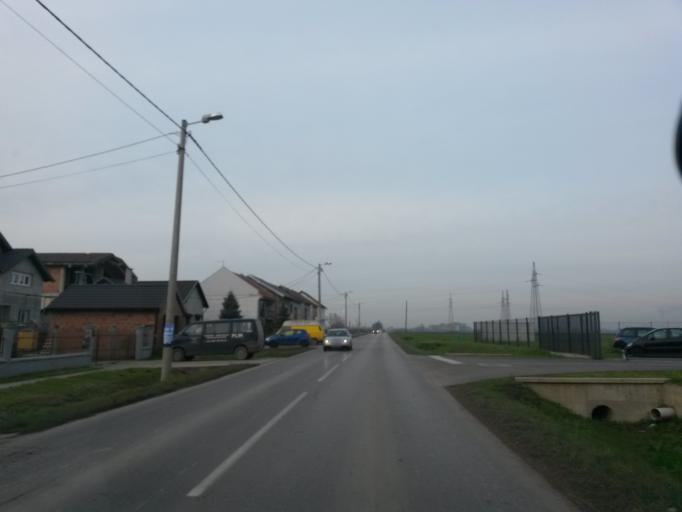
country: HR
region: Osjecko-Baranjska
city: Tenja
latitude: 45.5206
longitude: 18.7276
